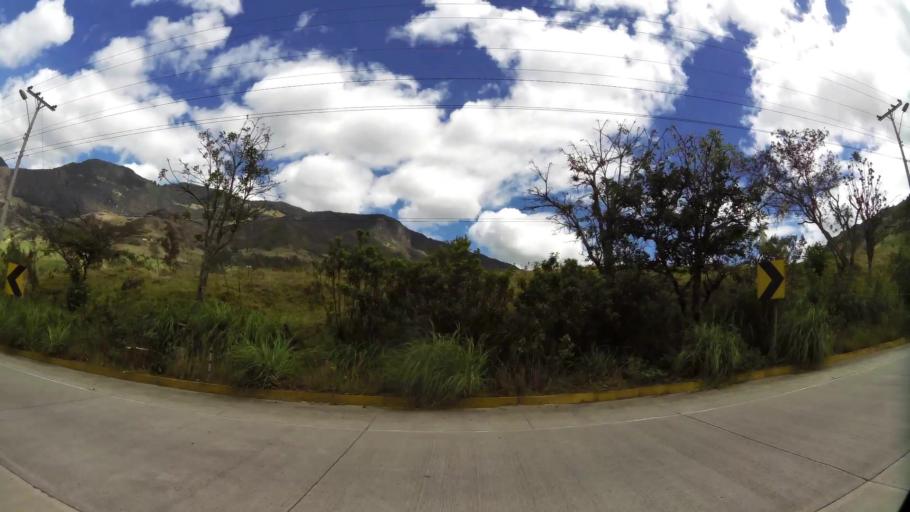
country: EC
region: Azuay
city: Cuenca
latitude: -3.1338
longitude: -79.1221
